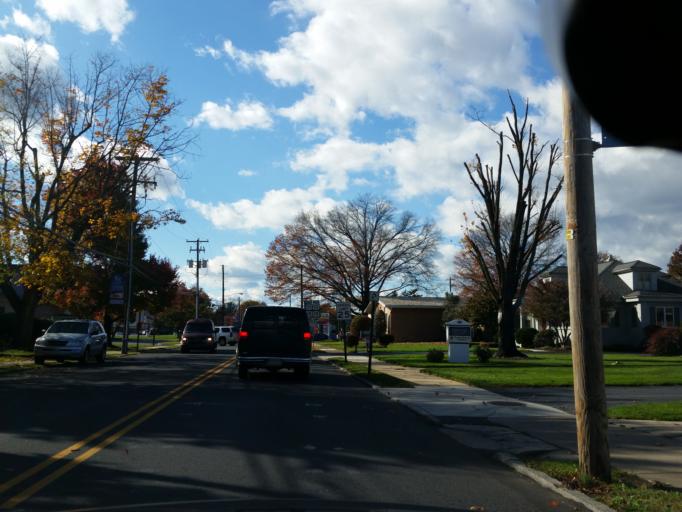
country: US
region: Pennsylvania
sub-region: Cumberland County
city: Camp Hill
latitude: 40.2401
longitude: -76.9321
